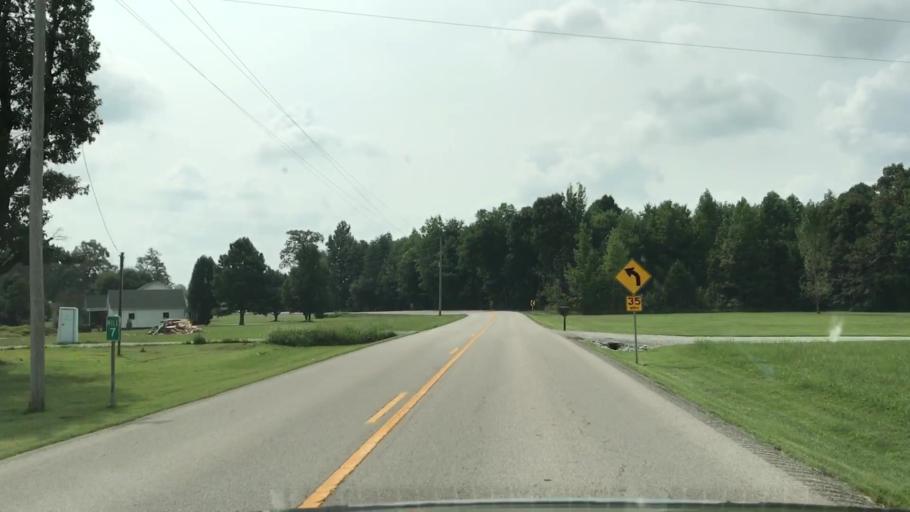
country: US
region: Kentucky
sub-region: Edmonson County
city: Brownsville
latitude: 37.1453
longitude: -86.1931
